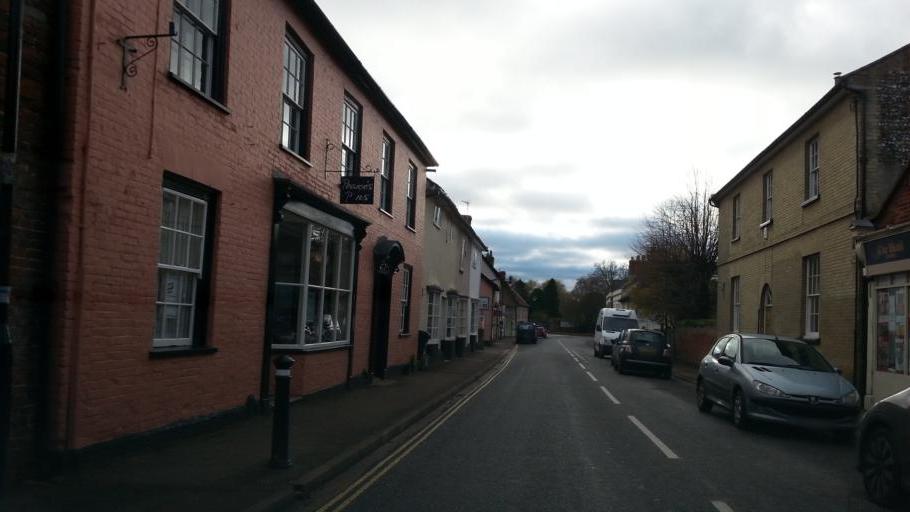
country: GB
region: England
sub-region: Suffolk
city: Ixworth
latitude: 52.2978
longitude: 0.8320
